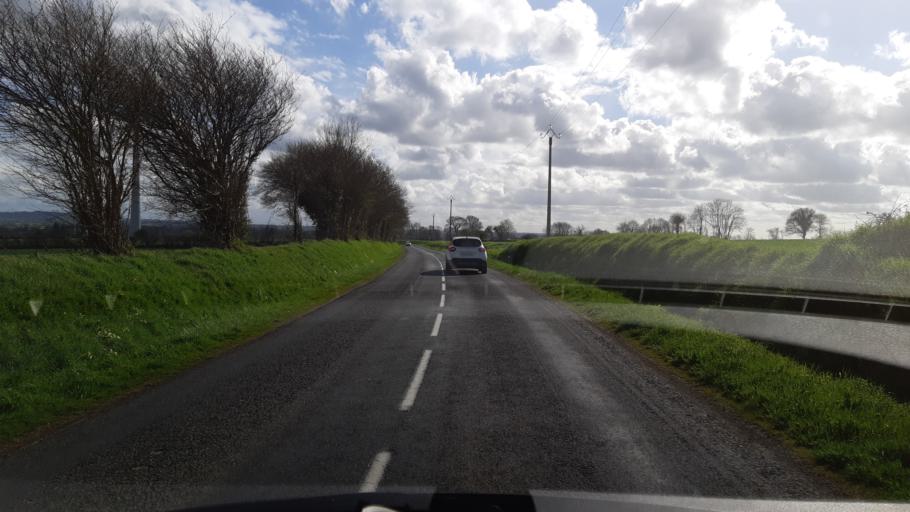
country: FR
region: Lower Normandy
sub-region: Departement de la Manche
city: Percy
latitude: 49.0219
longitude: -1.1594
